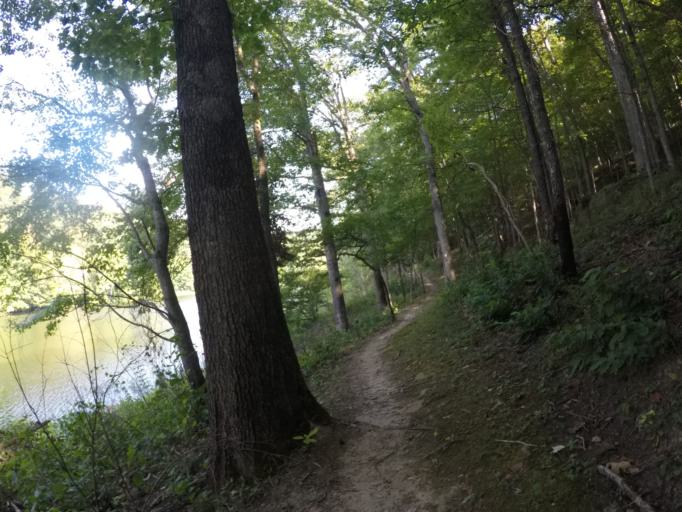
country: US
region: Ohio
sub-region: Lawrence County
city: Ironton
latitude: 38.6103
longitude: -82.6265
